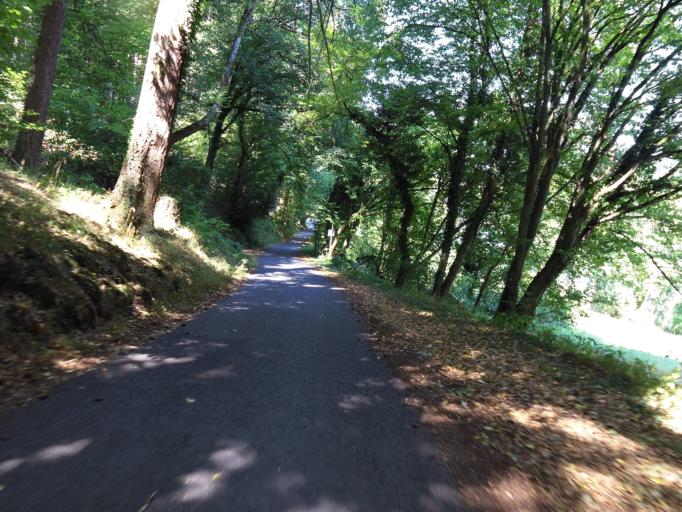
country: DE
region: Baden-Wuerttemberg
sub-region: Karlsruhe Region
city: Neunkirchen
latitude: 49.4204
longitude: 8.9998
